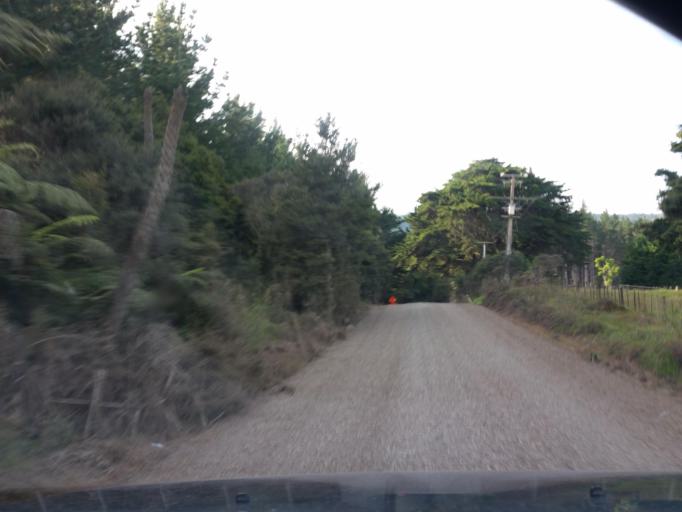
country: NZ
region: Northland
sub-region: Kaipara District
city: Dargaville
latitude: -35.7709
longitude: 173.7173
